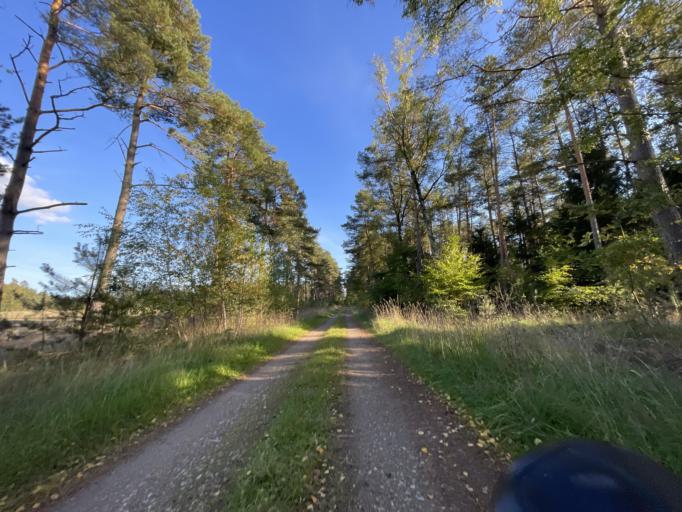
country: DE
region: Lower Saxony
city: Barendorf
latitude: 53.2075
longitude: 10.5014
